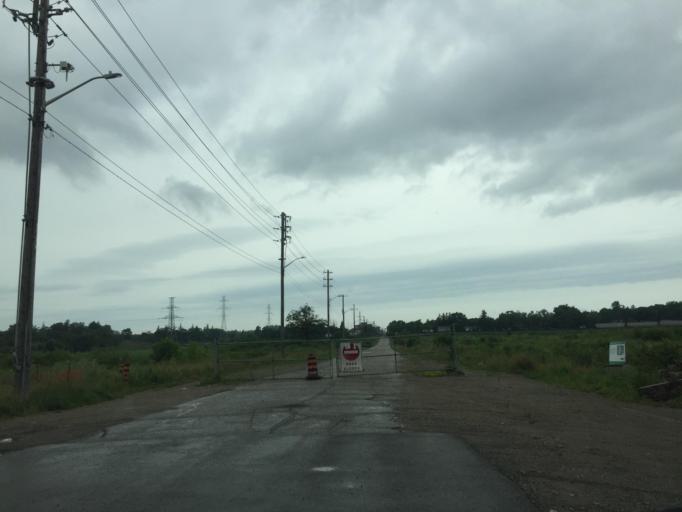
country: CA
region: Ontario
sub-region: Wellington County
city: Guelph
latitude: 43.5303
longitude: -80.2661
